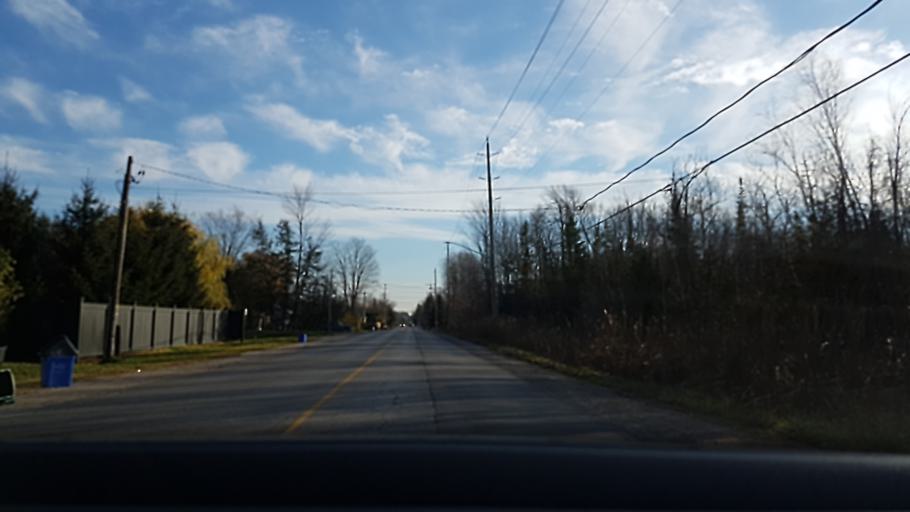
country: CA
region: Ontario
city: Innisfil
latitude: 44.3435
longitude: -79.5466
